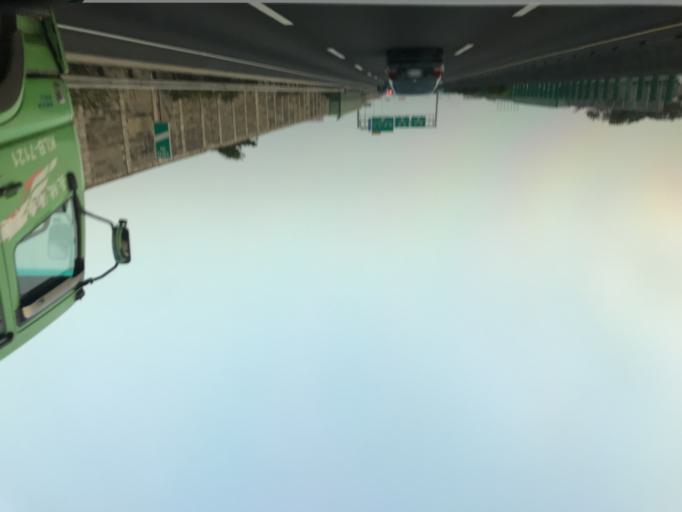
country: TW
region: Taiwan
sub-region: Yunlin
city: Douliu
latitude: 23.7248
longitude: 120.4745
